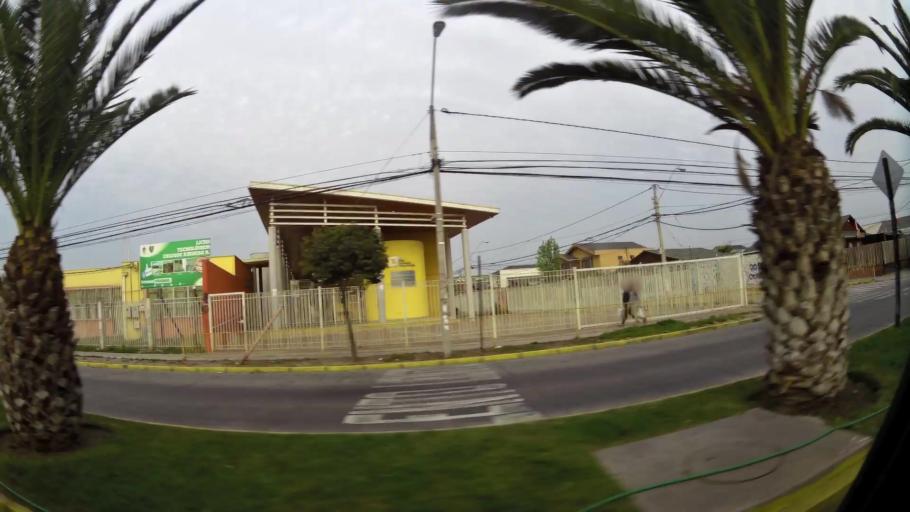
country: CL
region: Santiago Metropolitan
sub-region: Provincia de Santiago
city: Lo Prado
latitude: -33.5286
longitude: -70.7973
